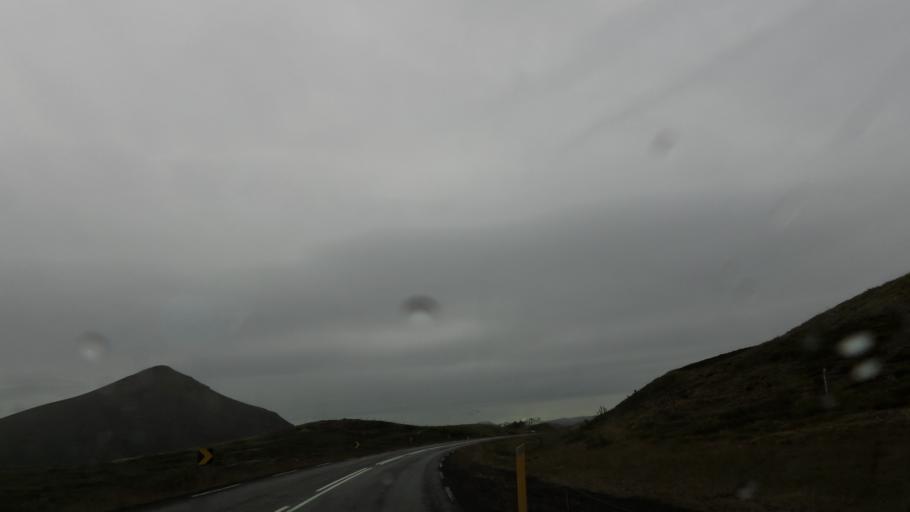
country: IS
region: Northeast
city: Laugar
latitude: 65.6124
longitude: -17.0861
